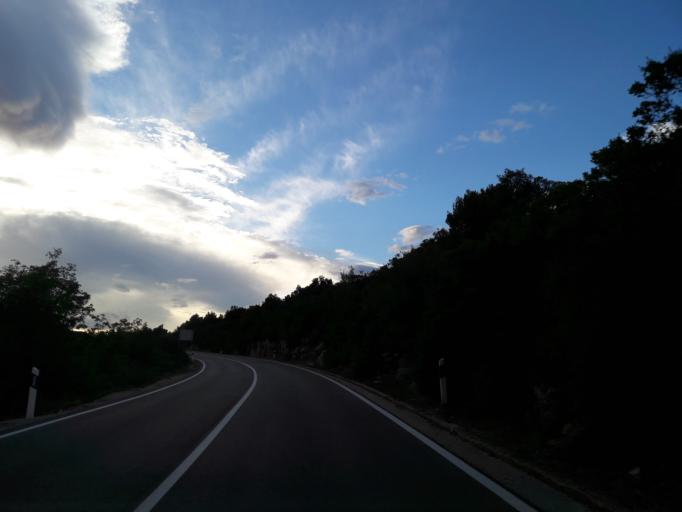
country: BA
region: Federation of Bosnia and Herzegovina
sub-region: Hercegovacko-Bosanski Kanton
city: Neum
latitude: 42.8870
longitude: 17.5033
